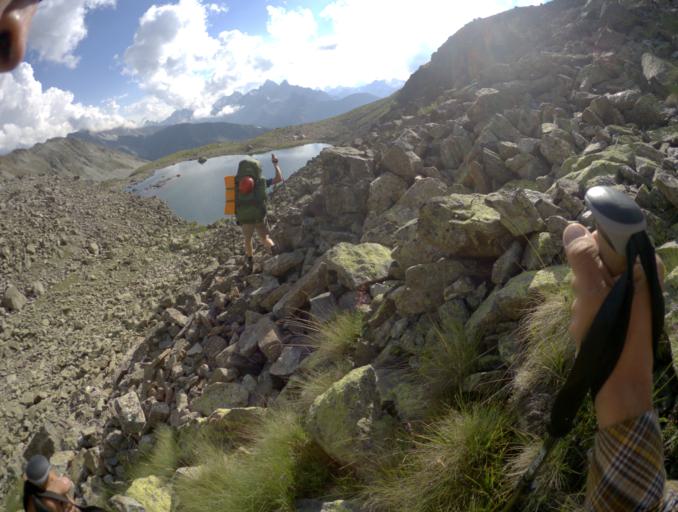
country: RU
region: Karachayevo-Cherkesiya
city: Uchkulan
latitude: 43.3150
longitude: 42.0699
